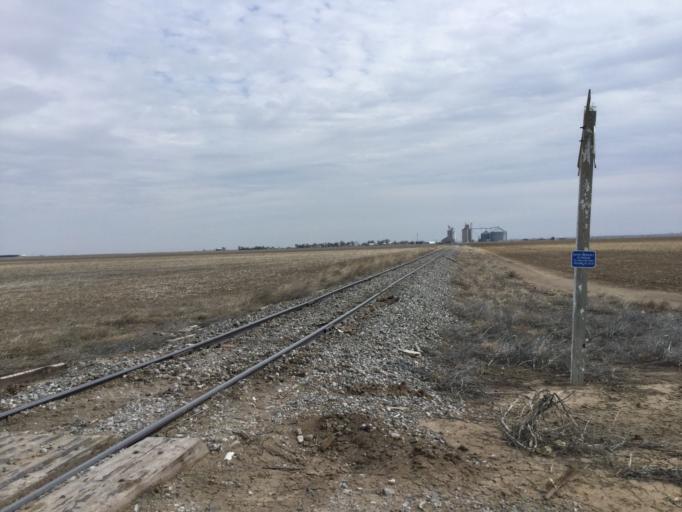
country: US
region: Kansas
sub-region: Stanton County
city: Johnson
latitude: 37.5623
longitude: -101.5811
